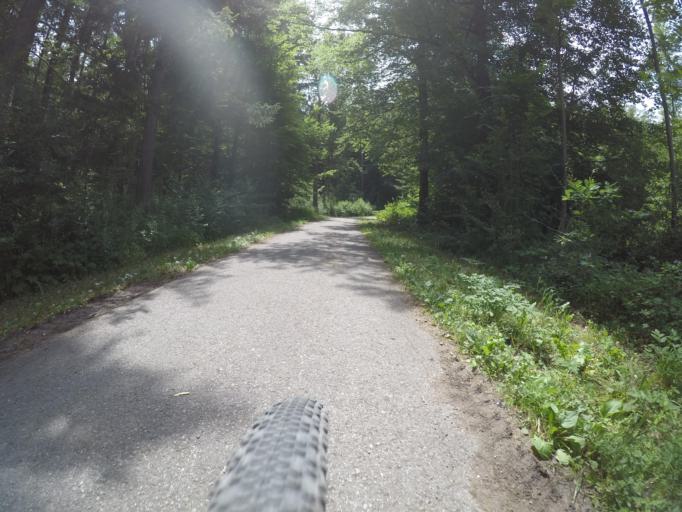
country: DE
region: Baden-Wuerttemberg
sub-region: Regierungsbezirk Stuttgart
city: Magstadt
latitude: 48.7376
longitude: 8.9977
